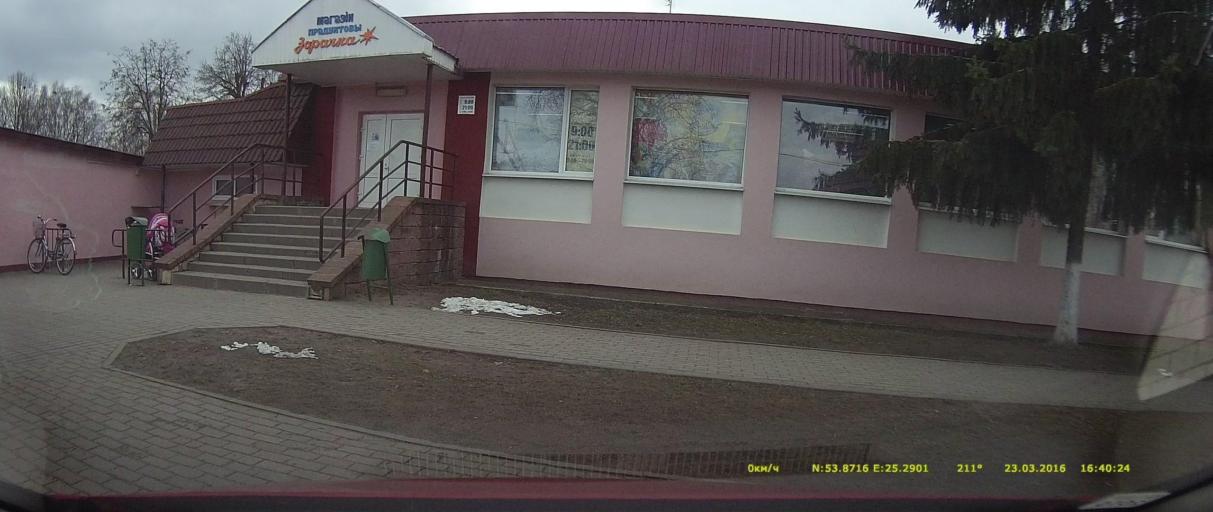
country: BY
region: Grodnenskaya
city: Lida
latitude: 53.8785
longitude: 25.2861
